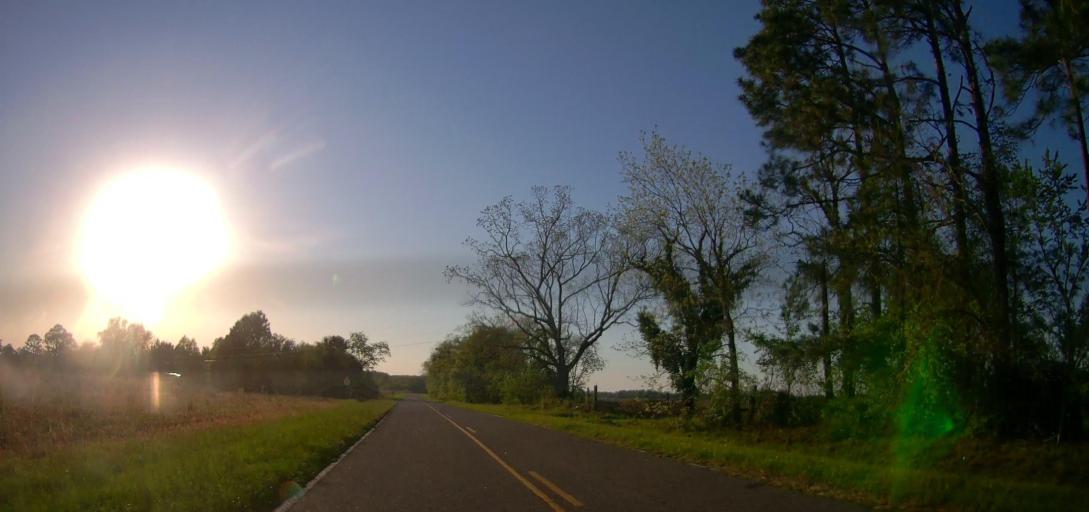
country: US
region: Georgia
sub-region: Ben Hill County
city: Fitzgerald
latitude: 31.6791
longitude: -83.2193
